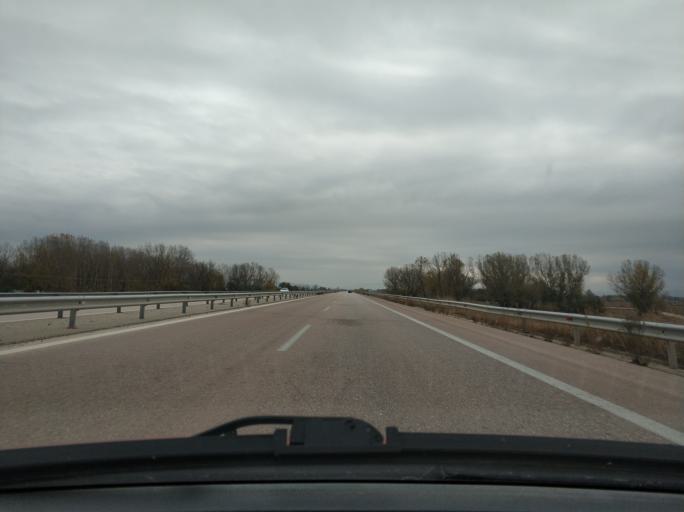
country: GR
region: Central Macedonia
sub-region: Nomos Thessalonikis
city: Kavallari
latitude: 40.7300
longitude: 23.0592
